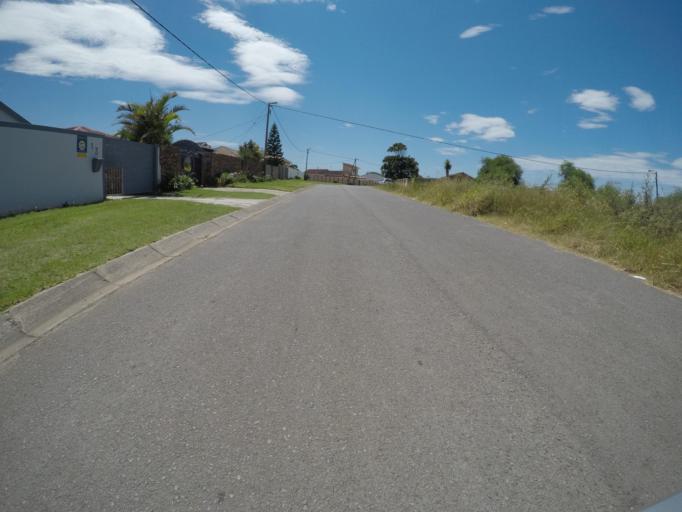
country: ZA
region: Eastern Cape
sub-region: Buffalo City Metropolitan Municipality
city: East London
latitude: -33.0437
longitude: 27.8668
